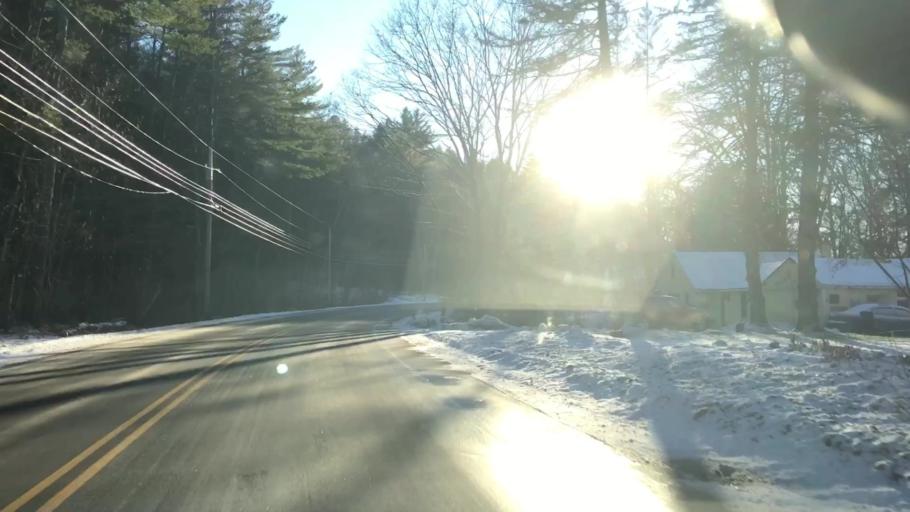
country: US
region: New Hampshire
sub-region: Grafton County
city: Orford
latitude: 43.9124
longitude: -72.1215
